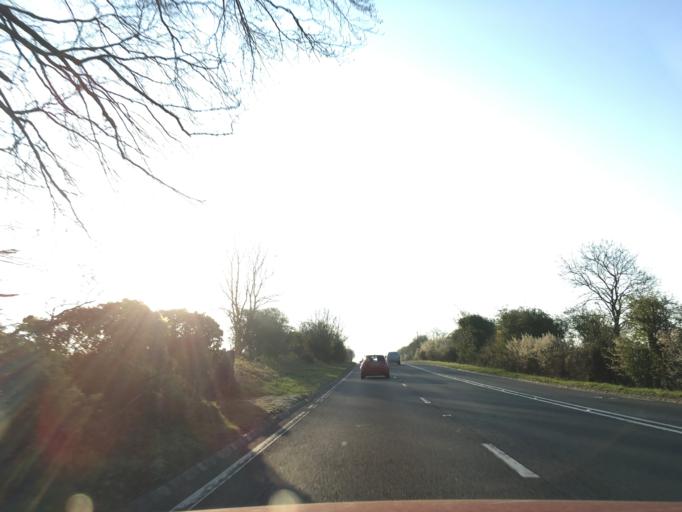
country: GB
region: England
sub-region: Gloucestershire
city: Shipton Village
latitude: 51.8599
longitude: -1.9534
